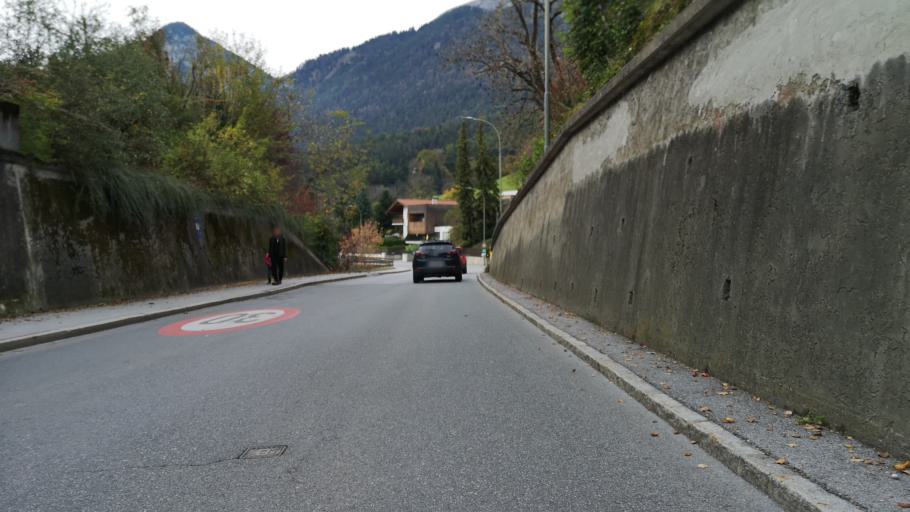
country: AT
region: Tyrol
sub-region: Innsbruck Stadt
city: Innsbruck
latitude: 47.2688
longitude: 11.3651
